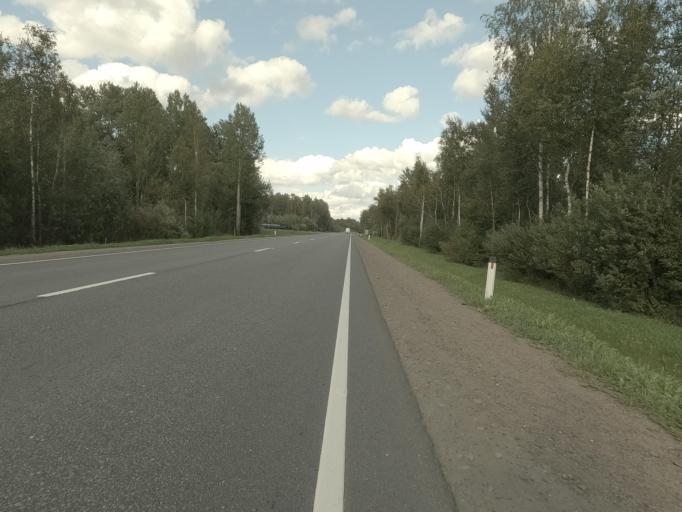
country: RU
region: Leningrad
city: Nikol'skoye
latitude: 59.6613
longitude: 30.8734
